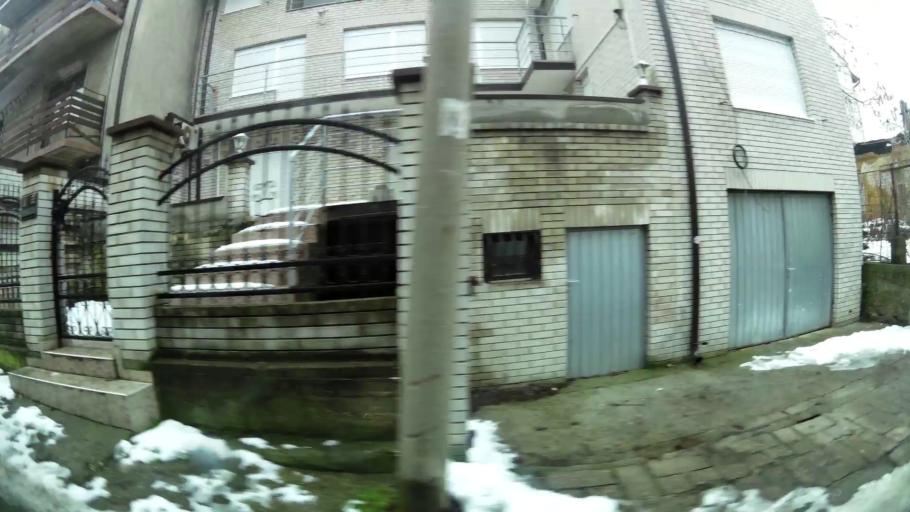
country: RS
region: Central Serbia
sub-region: Belgrade
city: Vozdovac
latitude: 44.7754
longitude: 20.4805
